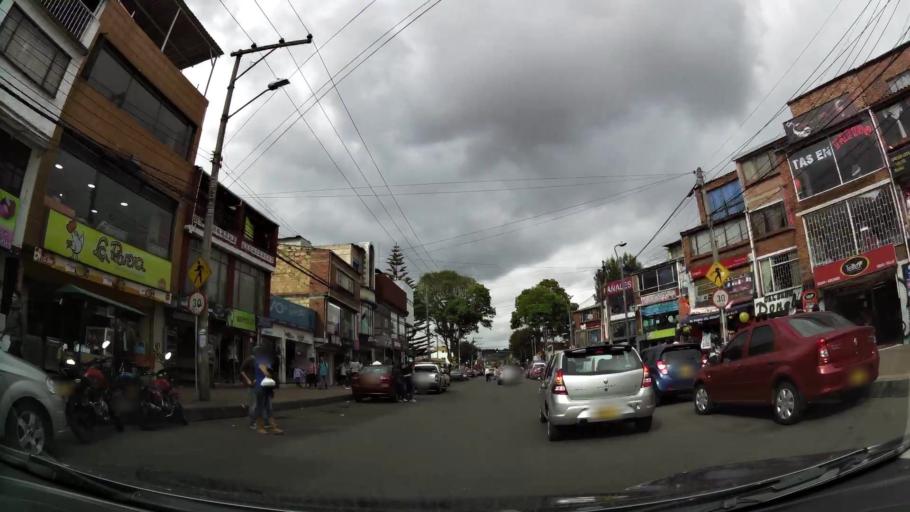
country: CO
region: Bogota D.C.
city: Barrio San Luis
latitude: 4.7077
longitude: -74.1057
